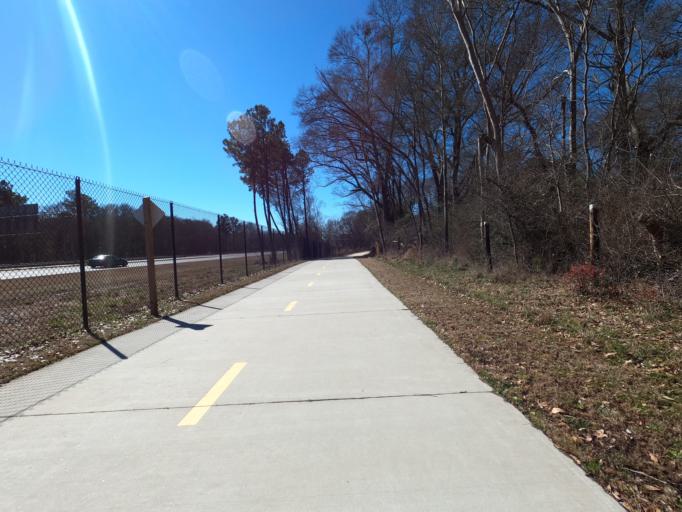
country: US
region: Georgia
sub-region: Clarke County
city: Athens
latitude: 33.9445
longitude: -83.3602
